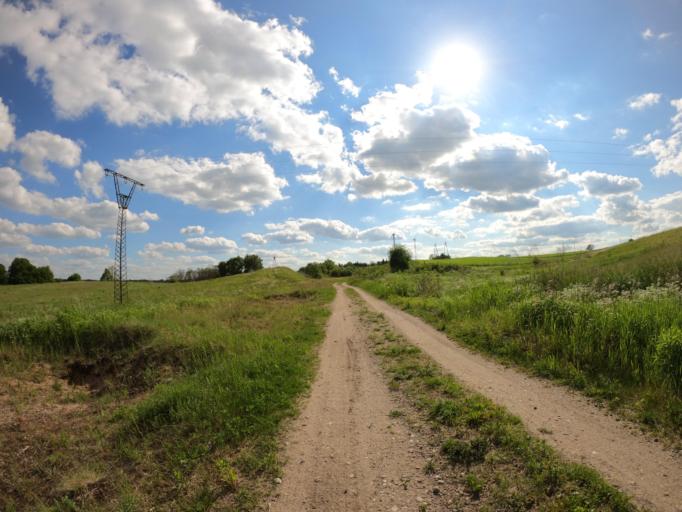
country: PL
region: Warmian-Masurian Voivodeship
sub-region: Powiat lidzbarski
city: Lidzbark Warminski
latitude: 54.1406
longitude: 20.6020
